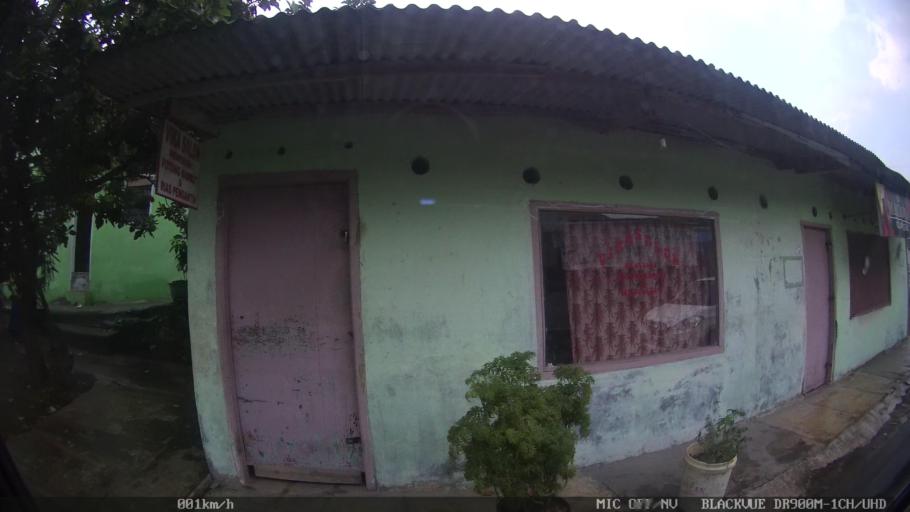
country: ID
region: Lampung
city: Bandarlampung
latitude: -5.4422
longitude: 105.2742
